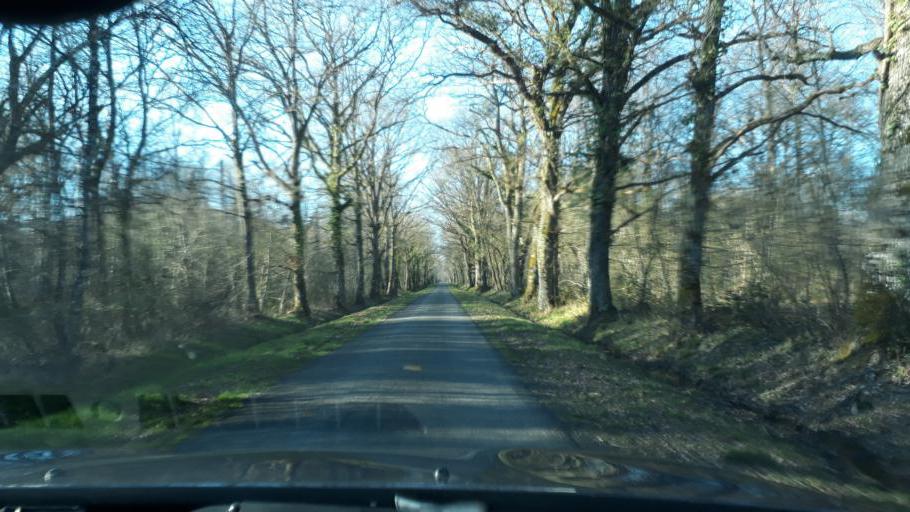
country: FR
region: Centre
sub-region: Departement du Loiret
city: Jouy-le-Potier
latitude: 47.7110
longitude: 1.8324
